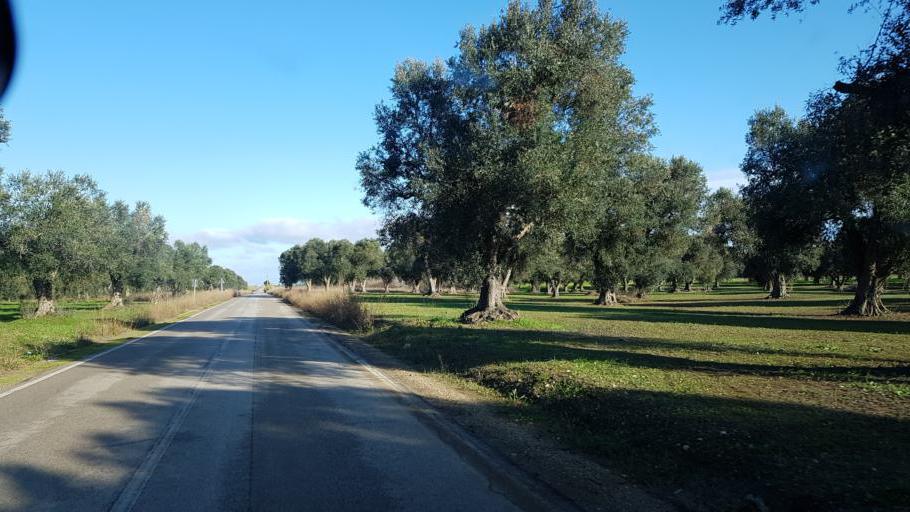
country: IT
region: Apulia
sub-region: Provincia di Brindisi
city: Tuturano
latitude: 40.5649
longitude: 17.9491
